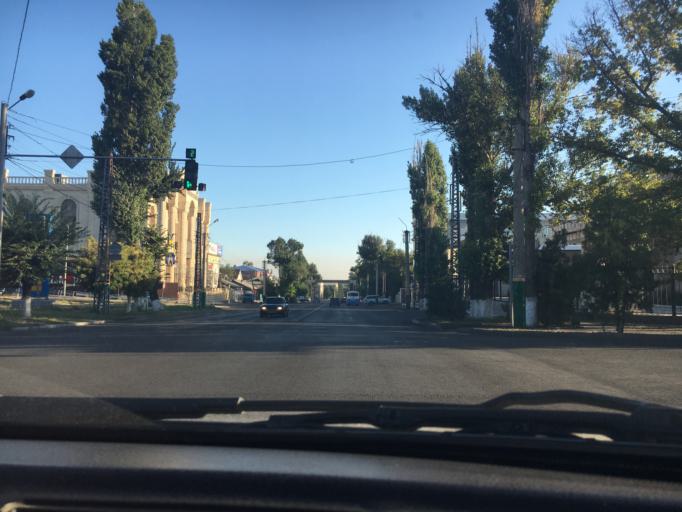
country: KZ
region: Zhambyl
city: Taraz
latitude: 42.8972
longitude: 71.3603
